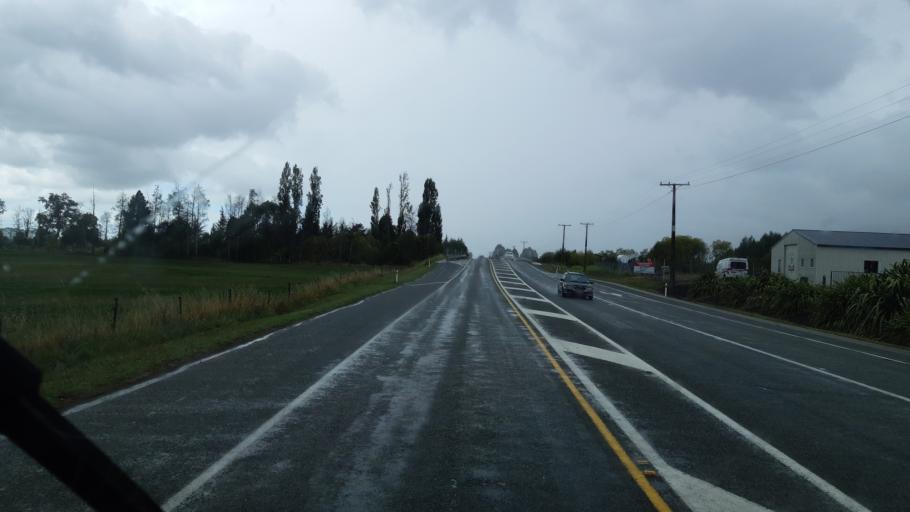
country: NZ
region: Tasman
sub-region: Tasman District
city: Brightwater
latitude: -41.3771
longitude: 173.1172
